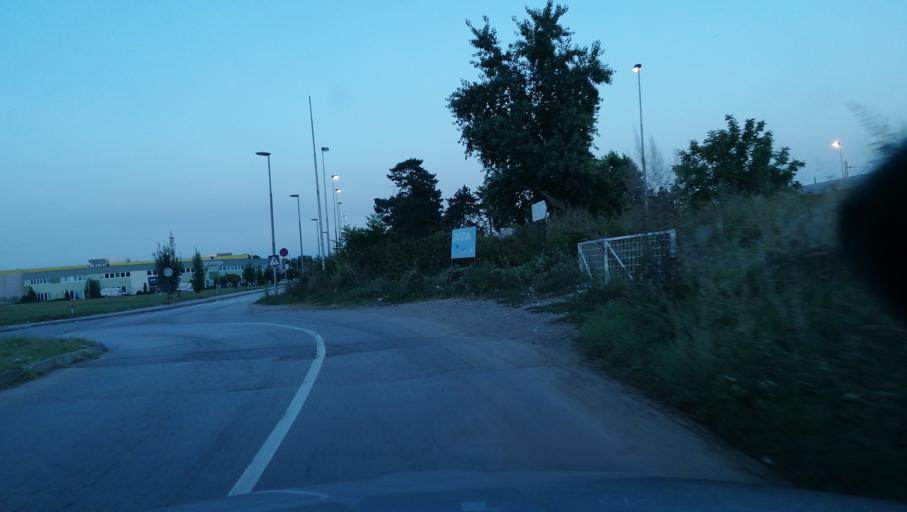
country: RS
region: Central Serbia
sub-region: Kolubarski Okrug
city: Valjevo
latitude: 44.2714
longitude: 19.9088
